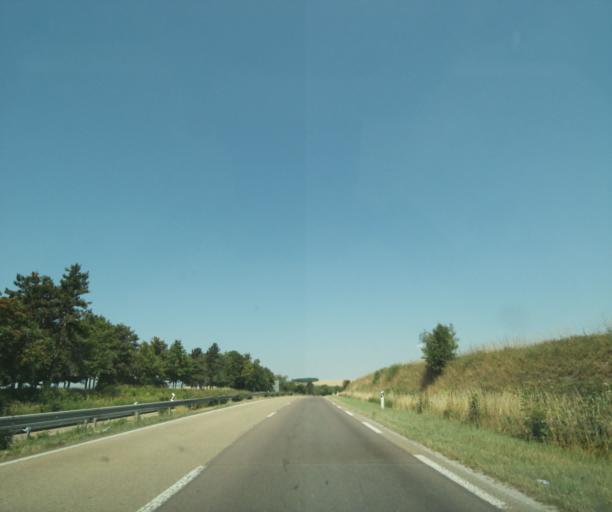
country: FR
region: Champagne-Ardenne
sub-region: Departement de la Marne
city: Fagnieres
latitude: 49.0393
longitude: 4.3124
